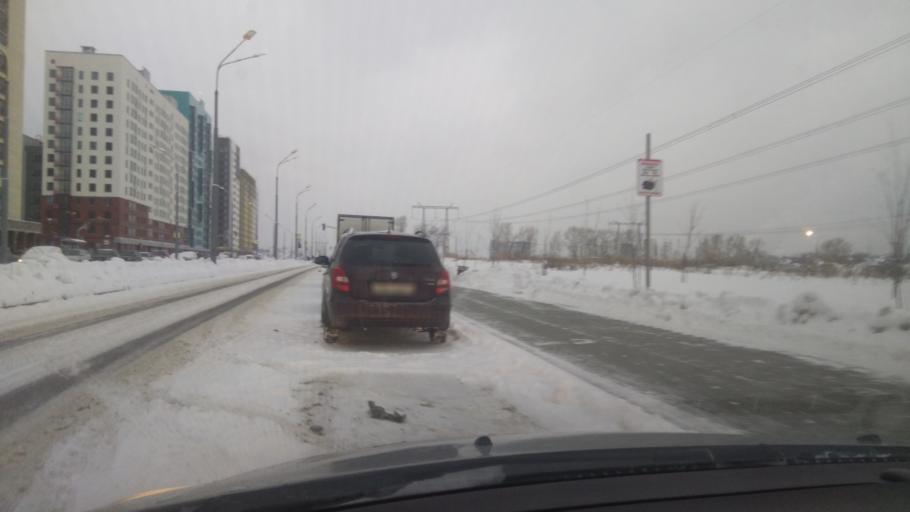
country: RU
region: Sverdlovsk
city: Sovkhoznyy
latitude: 56.7481
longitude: 60.5710
